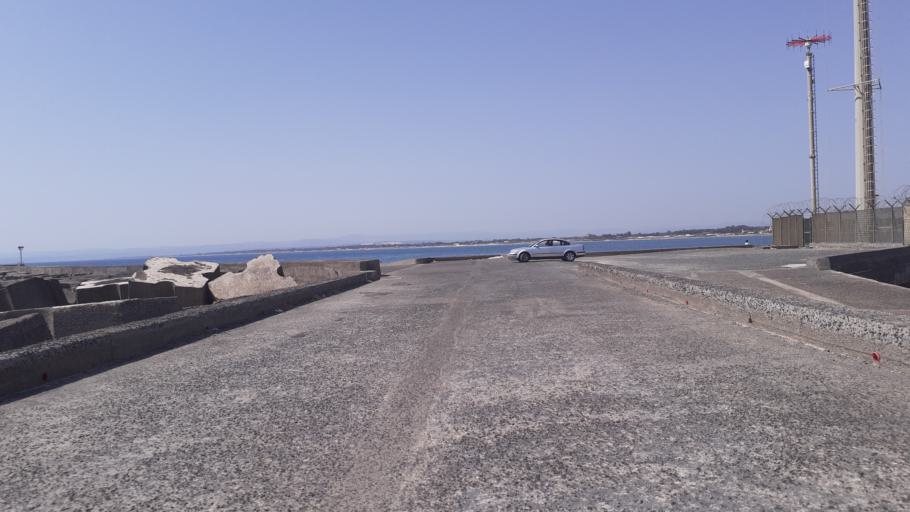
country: IT
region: Sicily
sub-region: Catania
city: Catania
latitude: 37.4872
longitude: 15.0994
